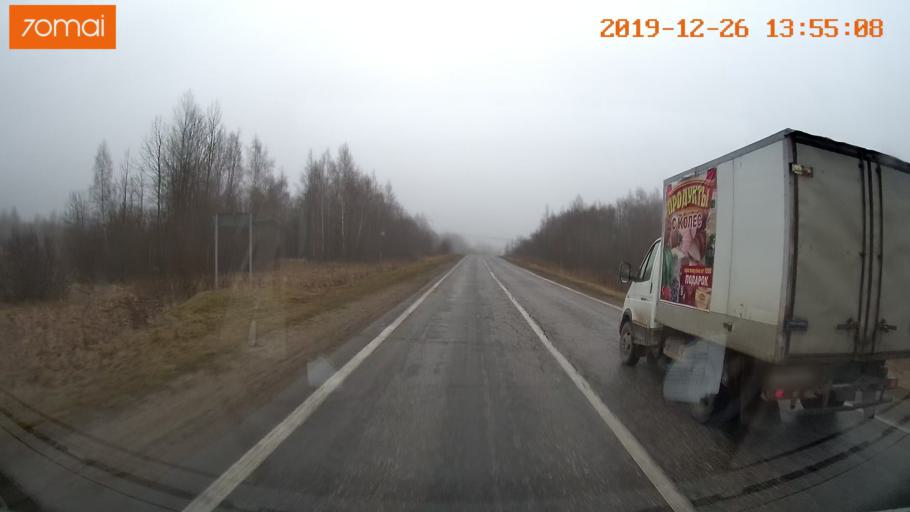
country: RU
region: Jaroslavl
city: Poshekhon'ye
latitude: 58.6067
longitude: 38.6434
